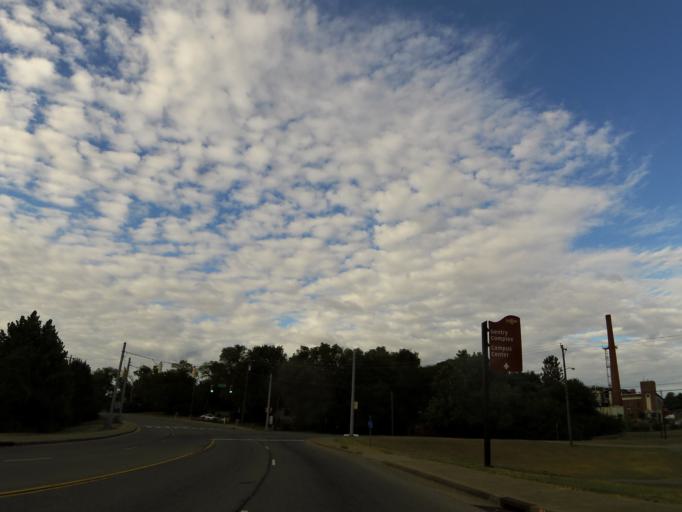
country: US
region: Tennessee
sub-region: Davidson County
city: Nashville
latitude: 36.1655
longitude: -86.8353
